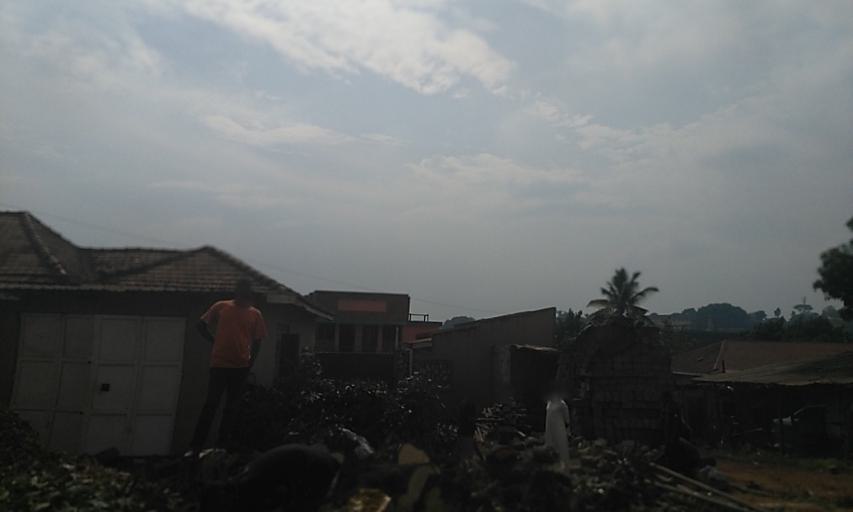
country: UG
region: Central Region
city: Kampala Central Division
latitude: 0.3096
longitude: 32.5642
